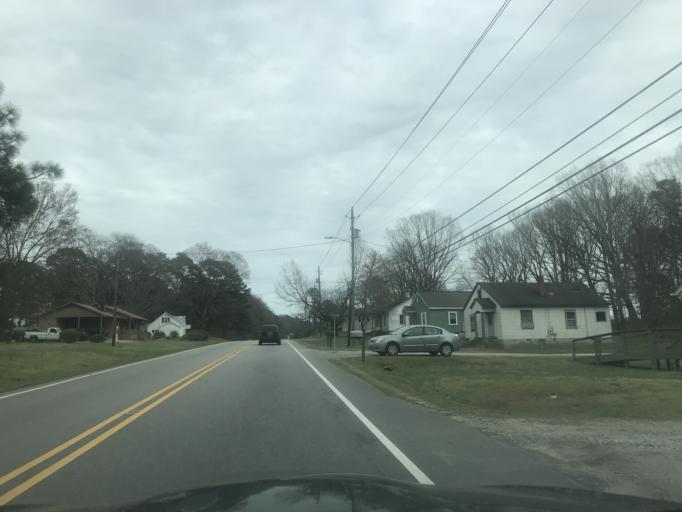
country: US
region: North Carolina
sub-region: Franklin County
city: Franklinton
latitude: 36.1024
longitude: -78.4327
